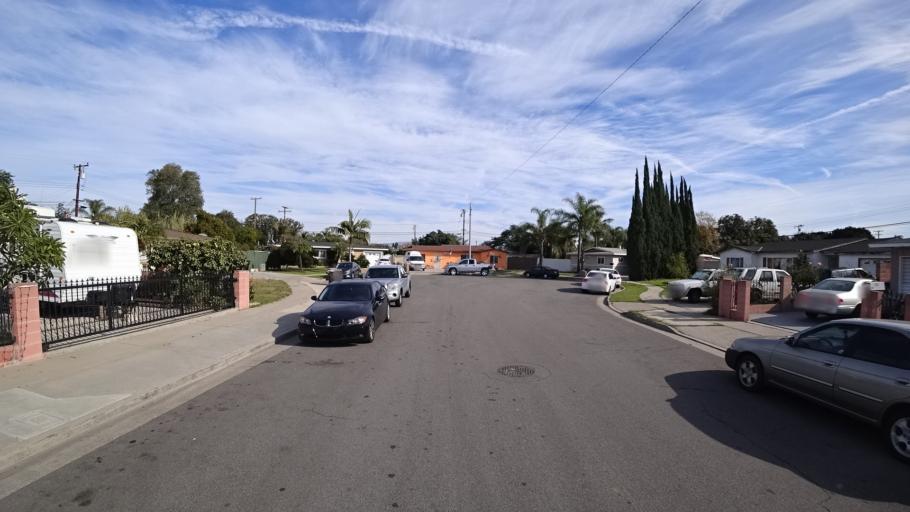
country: US
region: California
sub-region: Orange County
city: Garden Grove
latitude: 33.7624
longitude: -117.9081
